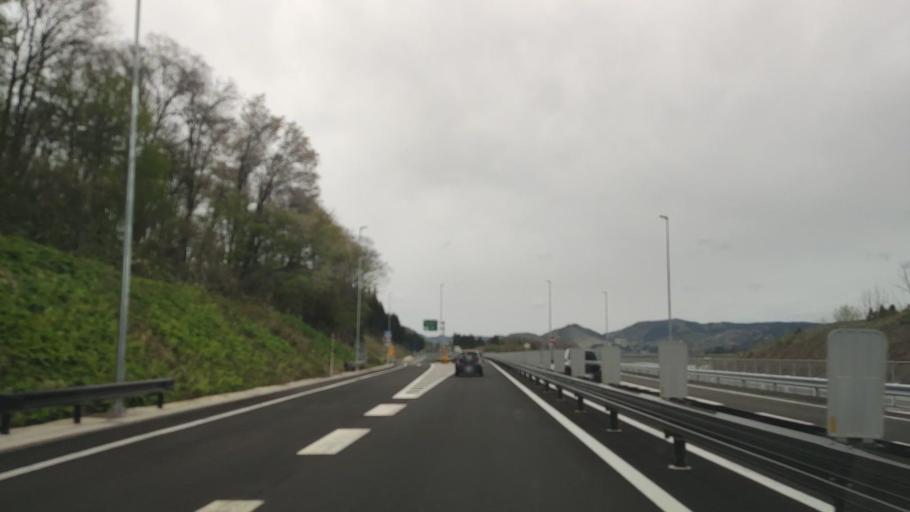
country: JP
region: Akita
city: Takanosu
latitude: 40.2058
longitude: 140.3177
